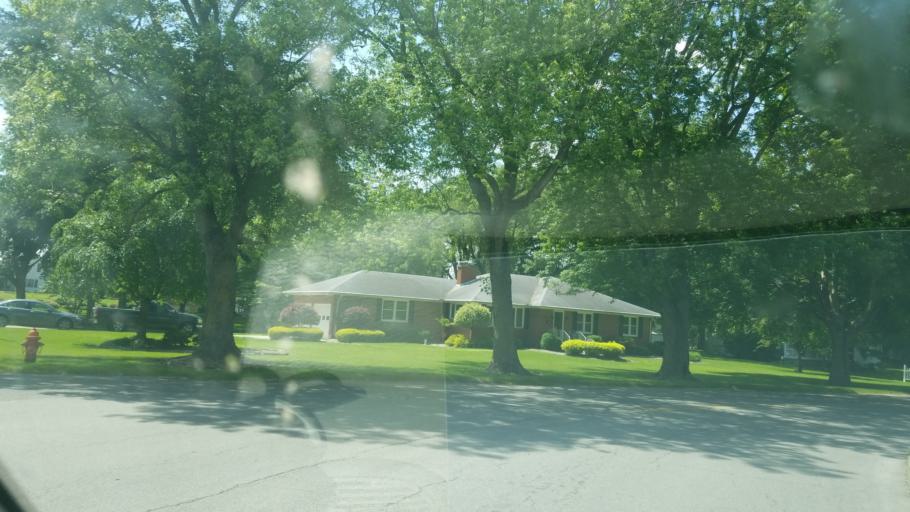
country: US
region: Ohio
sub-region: Wyandot County
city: Upper Sandusky
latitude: 40.8168
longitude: -83.2812
